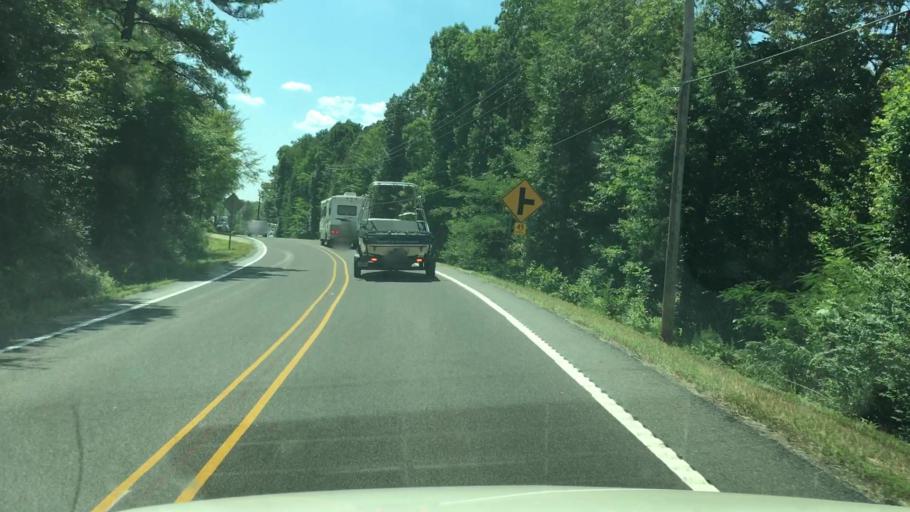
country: US
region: Arkansas
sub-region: Garland County
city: Piney
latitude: 34.5098
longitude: -93.1729
